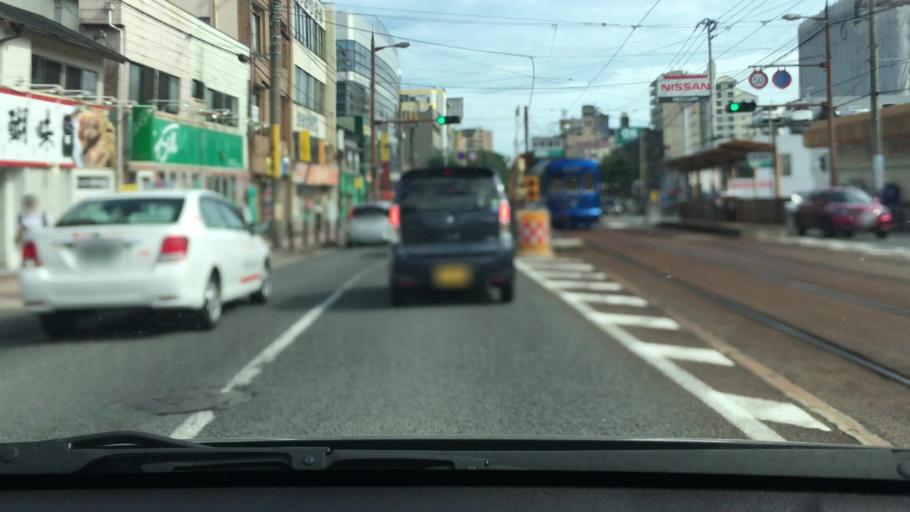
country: JP
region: Nagasaki
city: Obita
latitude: 32.7881
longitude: 129.8616
